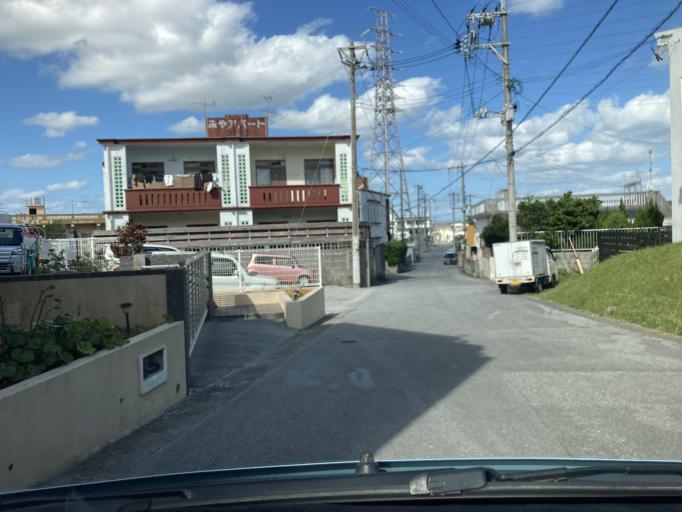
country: JP
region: Okinawa
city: Gushikawa
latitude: 26.3565
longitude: 127.8486
